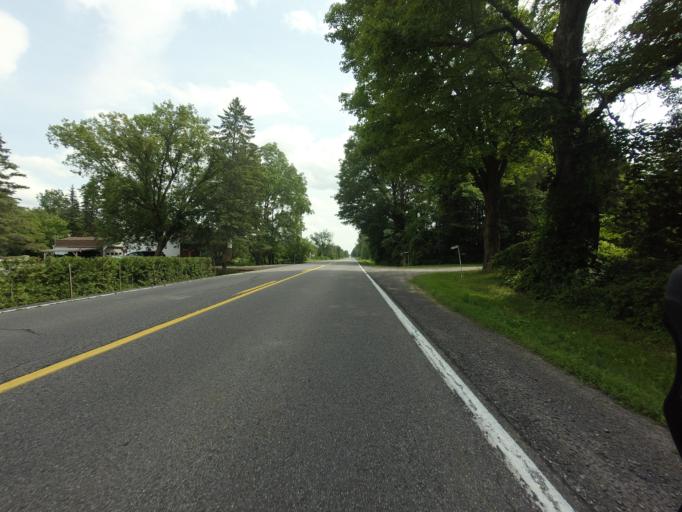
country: CA
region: Ontario
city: Ottawa
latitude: 45.2141
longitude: -75.5993
